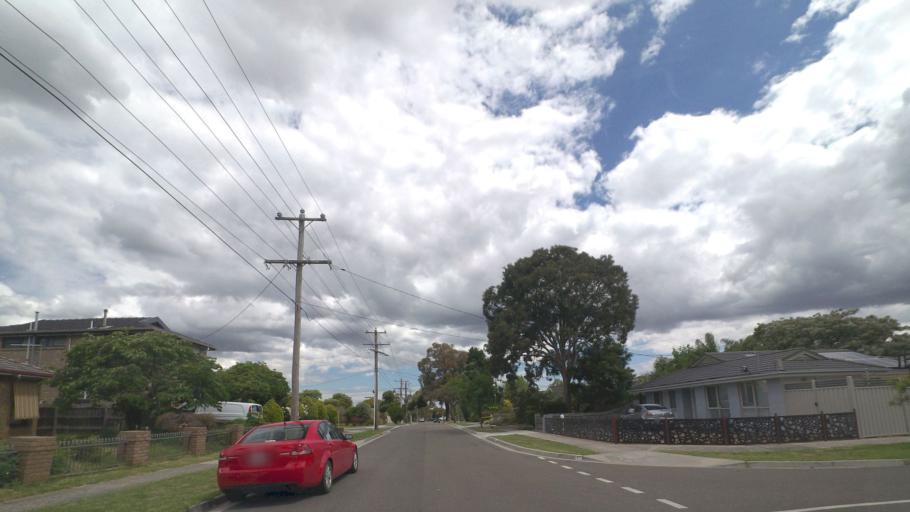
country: AU
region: Victoria
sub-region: Maroondah
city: Heathmont
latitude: -37.8500
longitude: 145.2406
